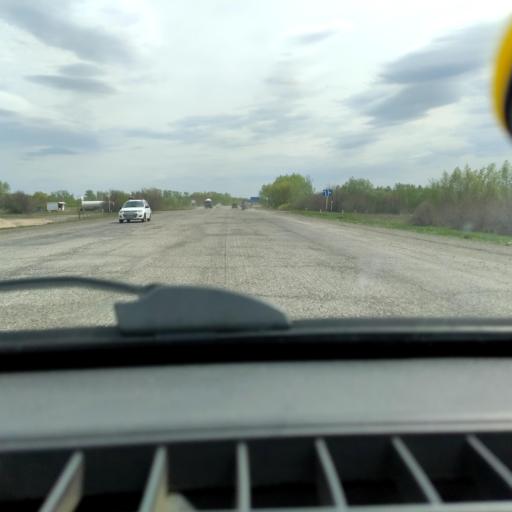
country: RU
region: Samara
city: Tol'yatti
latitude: 53.6652
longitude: 49.4205
